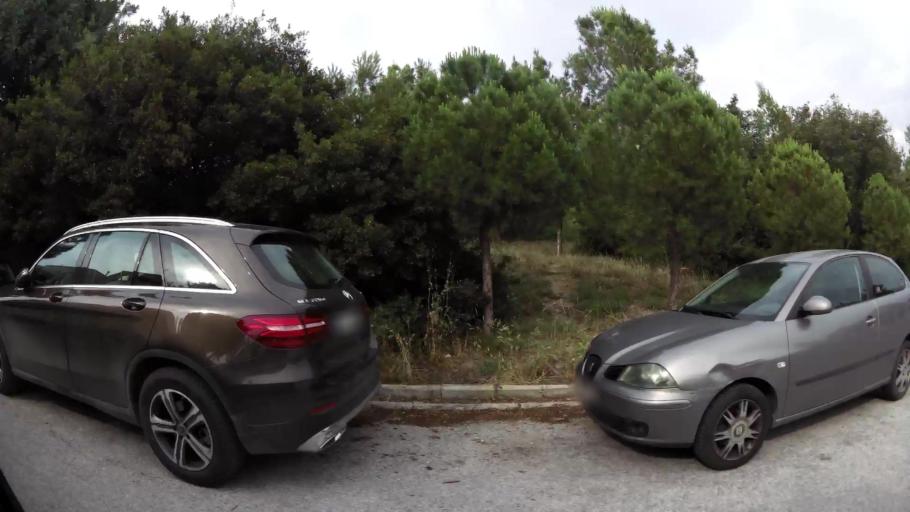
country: GR
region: Central Macedonia
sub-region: Nomos Thessalonikis
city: Oraiokastro
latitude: 40.7305
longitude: 22.9244
